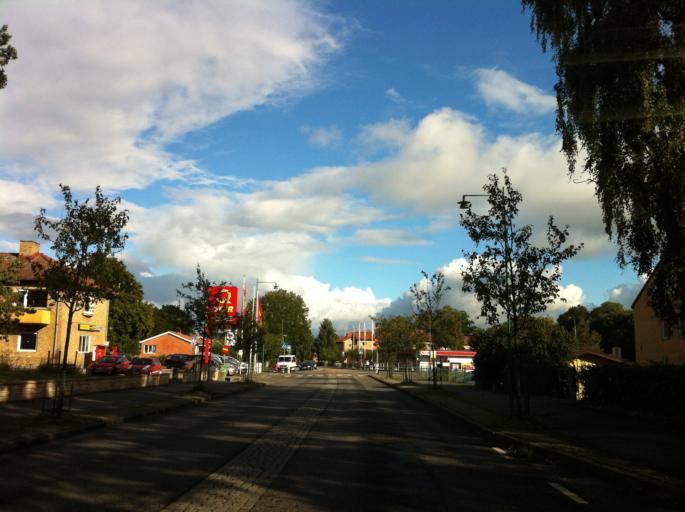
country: SE
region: Skane
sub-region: Hassleholms Kommun
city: Tormestorp
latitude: 56.1617
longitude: 13.6023
